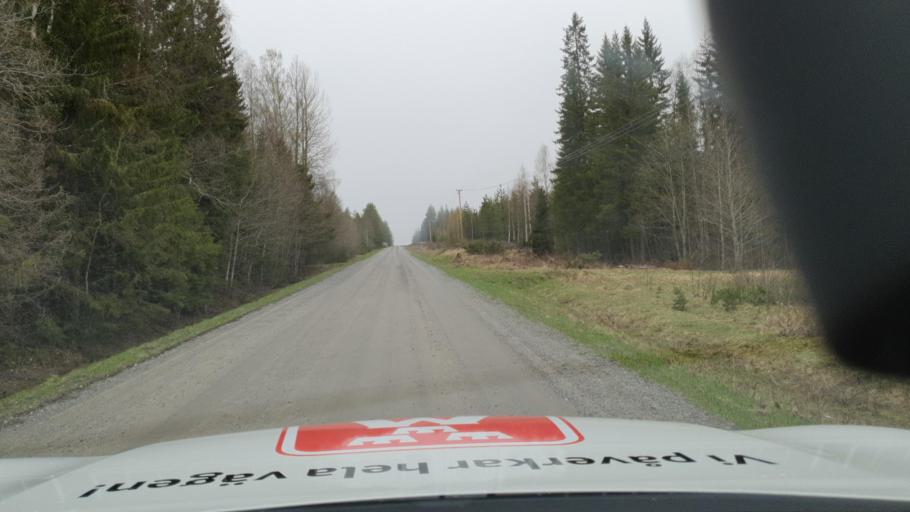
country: SE
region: Vaesterbotten
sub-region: Nordmalings Kommun
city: Nordmaling
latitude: 63.7390
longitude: 19.5035
